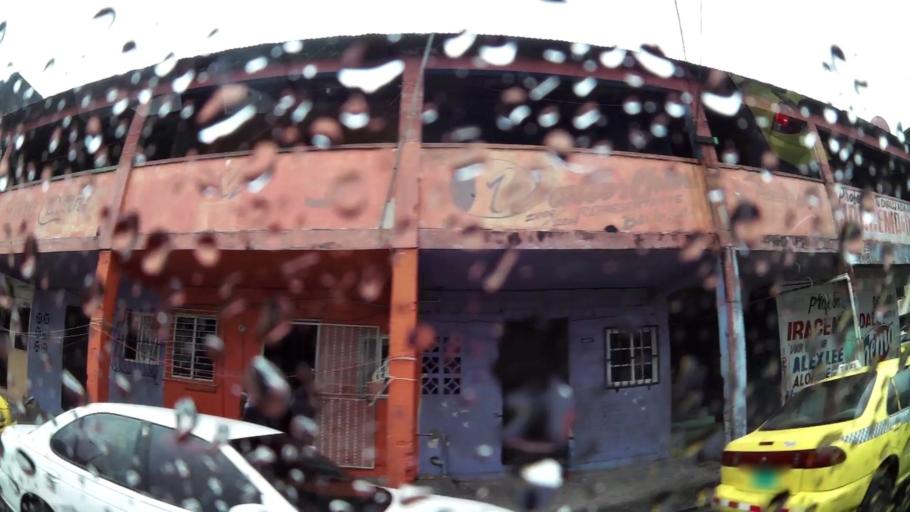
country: PA
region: Colon
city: Colon
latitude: 9.3538
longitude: -79.9017
